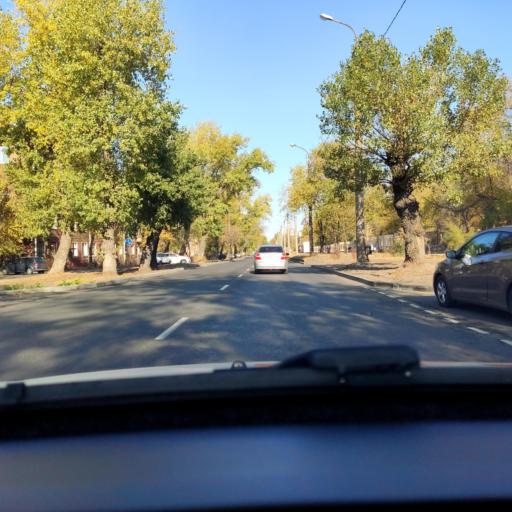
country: RU
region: Voronezj
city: Voronezh
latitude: 51.6398
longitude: 39.2397
